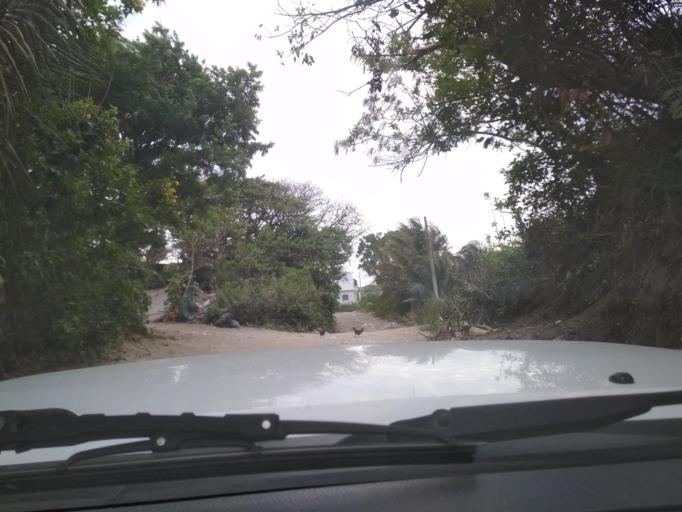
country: MX
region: Veracruz
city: Anton Lizardo
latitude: 19.0550
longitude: -95.9925
